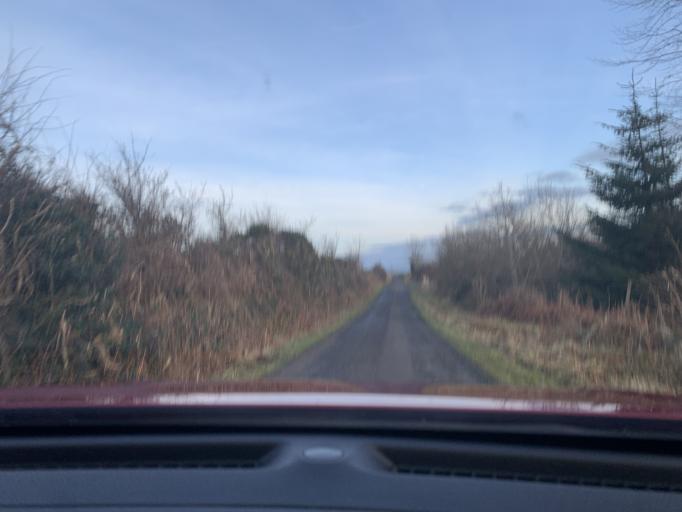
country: IE
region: Connaught
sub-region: Sligo
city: Strandhill
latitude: 54.1774
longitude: -8.6298
